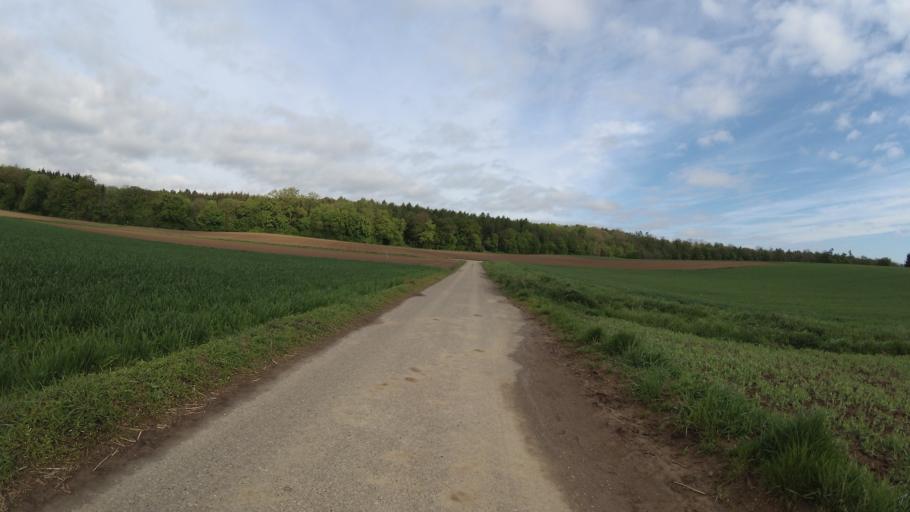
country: DE
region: Baden-Wuerttemberg
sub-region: Regierungsbezirk Stuttgart
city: Neuenstadt am Kocher
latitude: 49.2248
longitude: 9.2984
